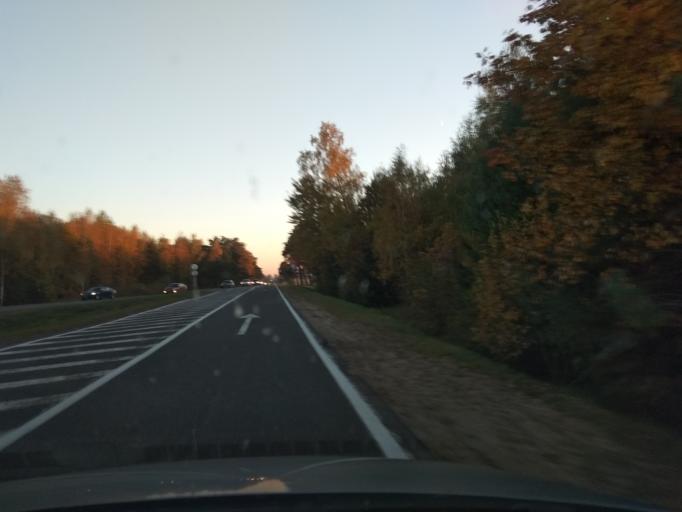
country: BY
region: Minsk
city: Haradzyeya
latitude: 53.3762
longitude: 26.5091
